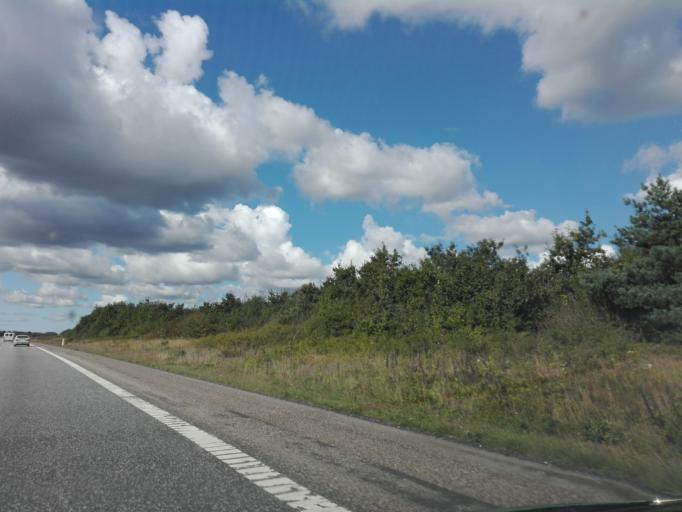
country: DK
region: North Denmark
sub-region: Mariagerfjord Kommune
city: Hobro
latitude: 56.5709
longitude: 9.8516
